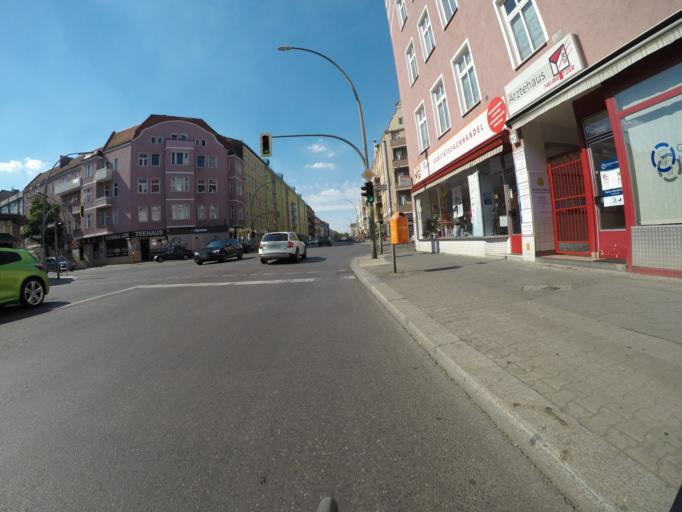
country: DE
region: Berlin
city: Britz
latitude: 52.4644
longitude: 13.4332
